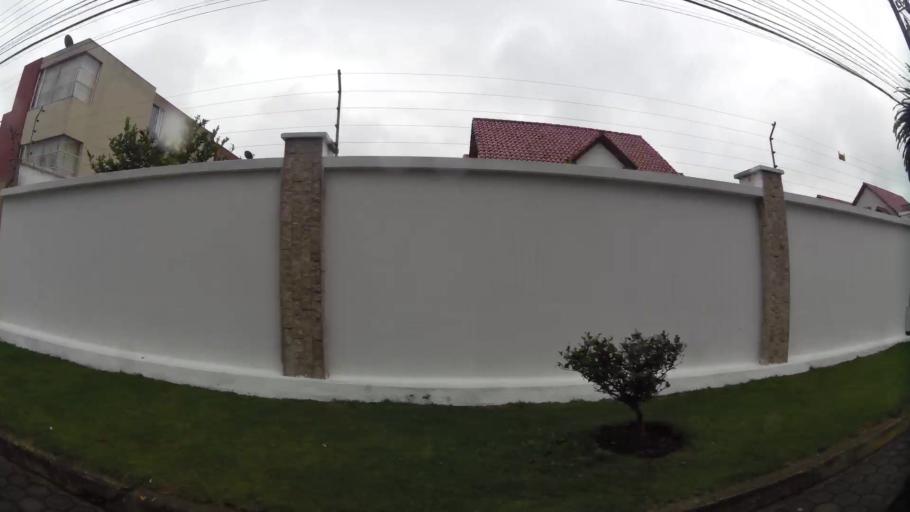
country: EC
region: Pichincha
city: Sangolqui
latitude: -0.2790
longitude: -78.4652
